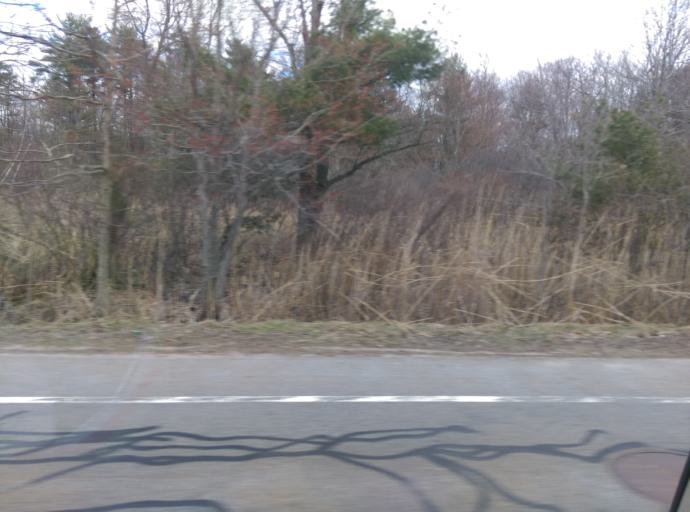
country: US
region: Massachusetts
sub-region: Essex County
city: Amesbury
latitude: 42.8512
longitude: -70.8988
